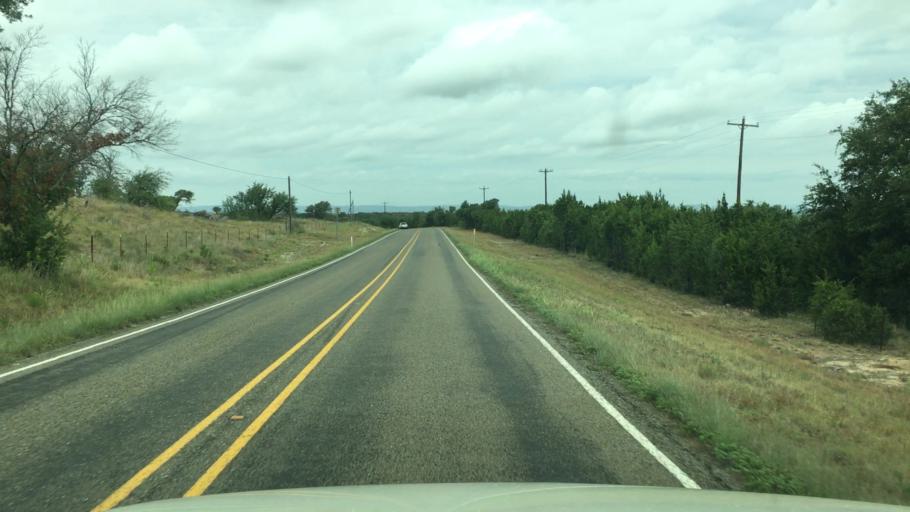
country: US
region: Texas
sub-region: Llano County
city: Horseshoe Bay
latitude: 30.4594
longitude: -98.4004
